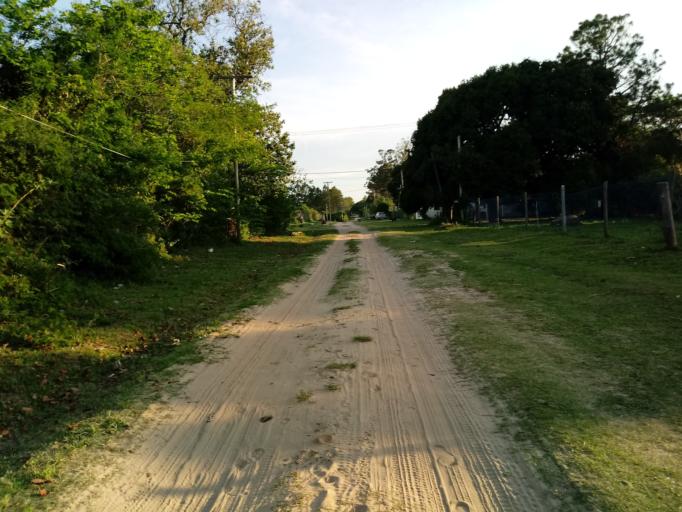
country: AR
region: Corrientes
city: San Luis del Palmar
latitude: -27.4516
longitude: -58.6572
